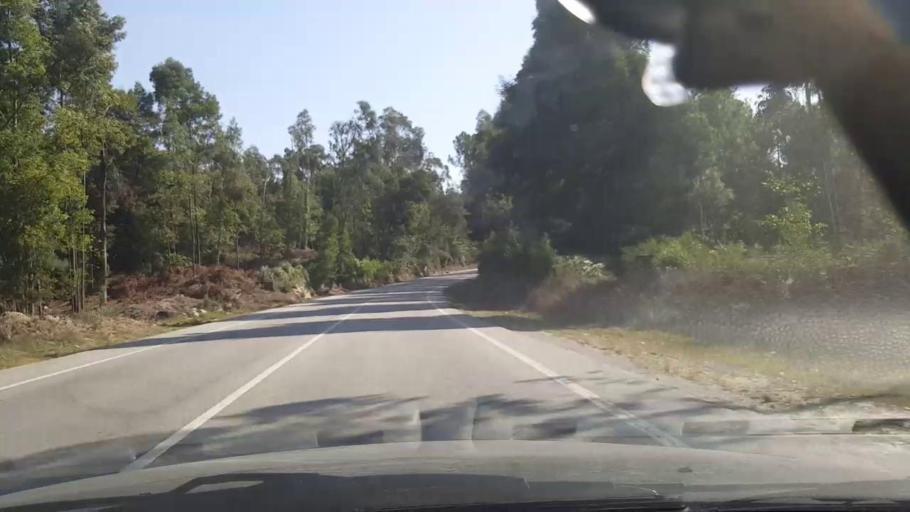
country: PT
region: Porto
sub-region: Vila do Conde
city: Arvore
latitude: 41.3571
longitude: -8.6841
